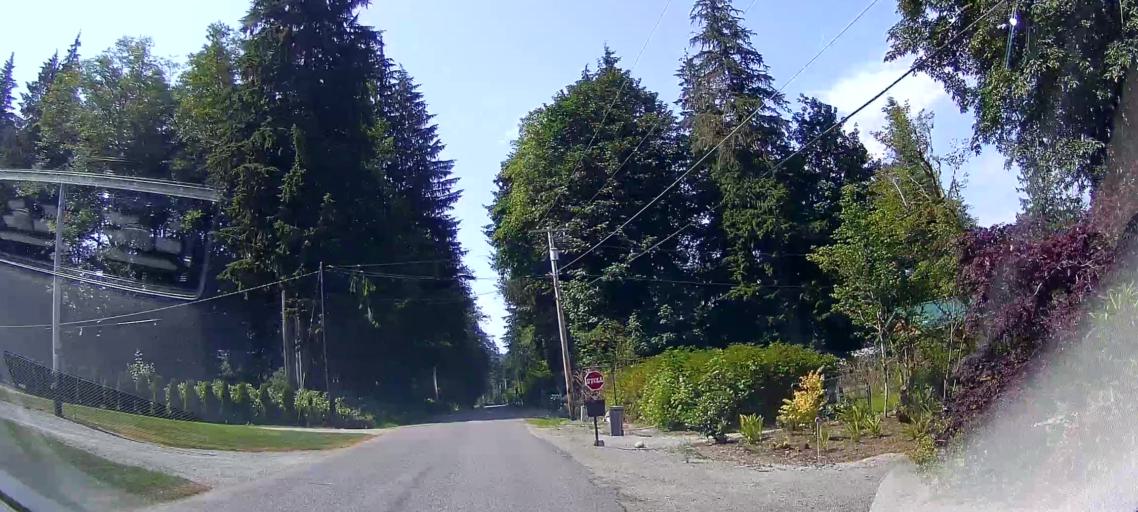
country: US
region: Washington
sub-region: Snohomish County
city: Arlington Heights
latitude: 48.3204
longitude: -122.0318
